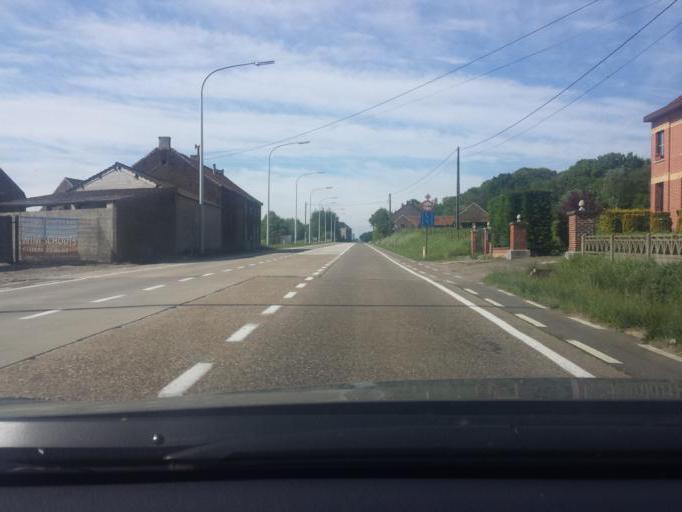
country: BE
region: Flanders
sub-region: Provincie Vlaams-Brabant
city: Diest
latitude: 50.9633
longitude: 5.0265
